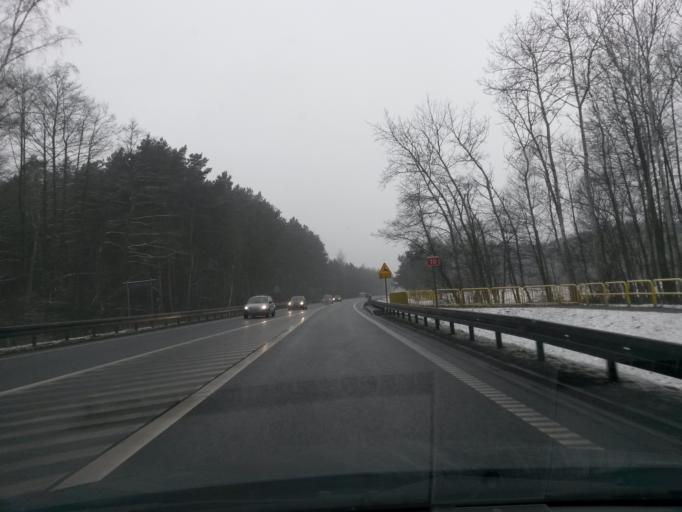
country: PL
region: Kujawsko-Pomorskie
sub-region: Powiat bydgoski
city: Solec Kujawski
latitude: 53.0612
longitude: 18.1837
